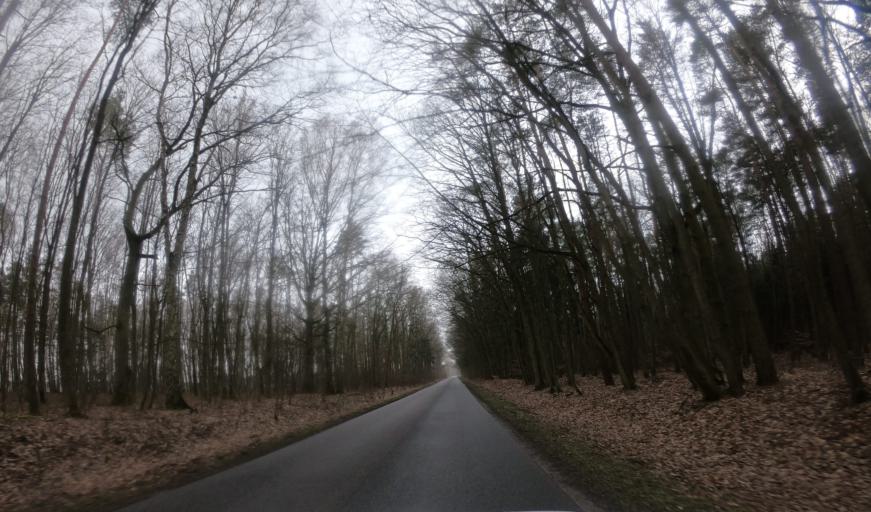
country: PL
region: West Pomeranian Voivodeship
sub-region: Powiat kamienski
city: Swierzno
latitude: 53.9255
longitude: 14.8878
